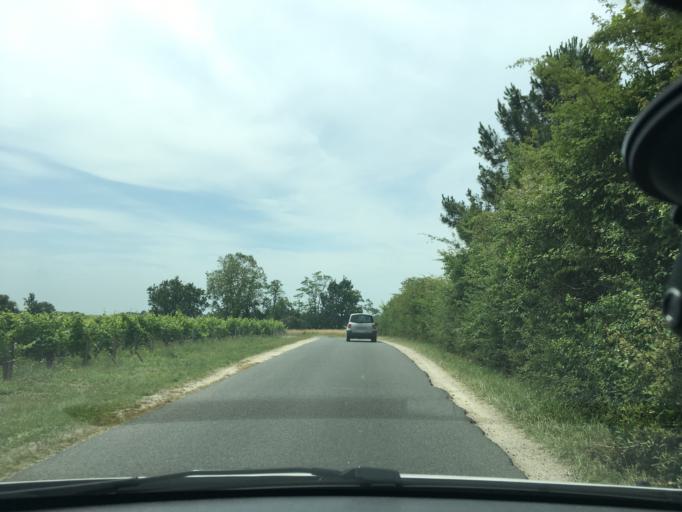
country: FR
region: Aquitaine
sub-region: Departement de la Gironde
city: Listrac-Medoc
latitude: 45.0618
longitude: -0.8024
